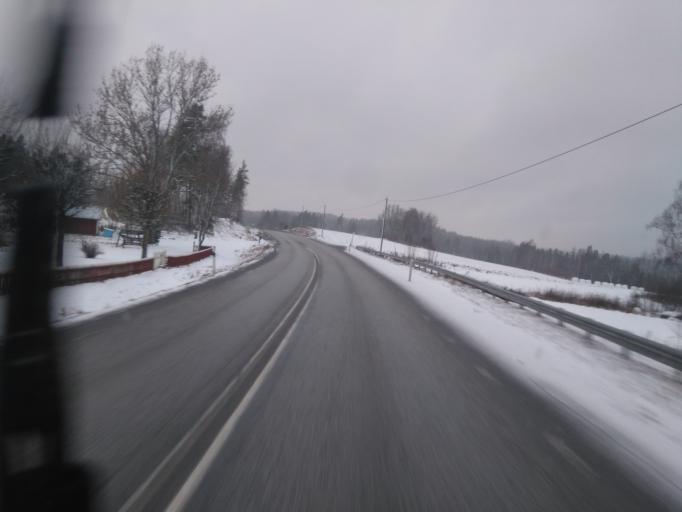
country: SE
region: Joenkoeping
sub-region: Eksjo Kommun
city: Eksjoe
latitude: 57.6411
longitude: 15.0816
